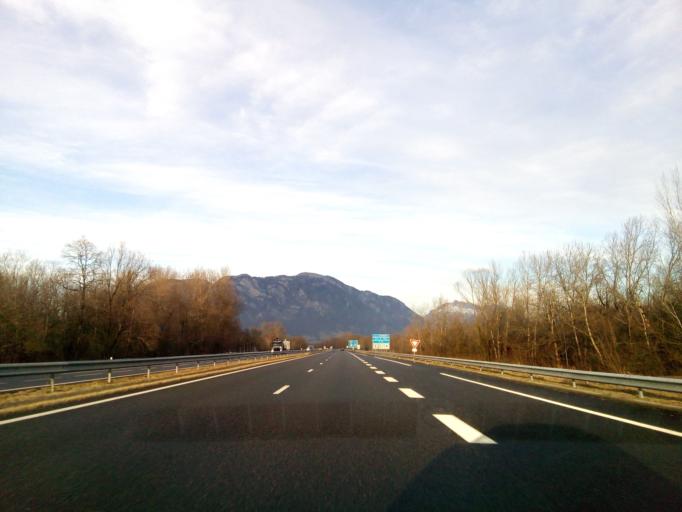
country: FR
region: Rhone-Alpes
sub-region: Departement de l'Isere
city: Chapareillan
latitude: 45.4616
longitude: 6.0109
